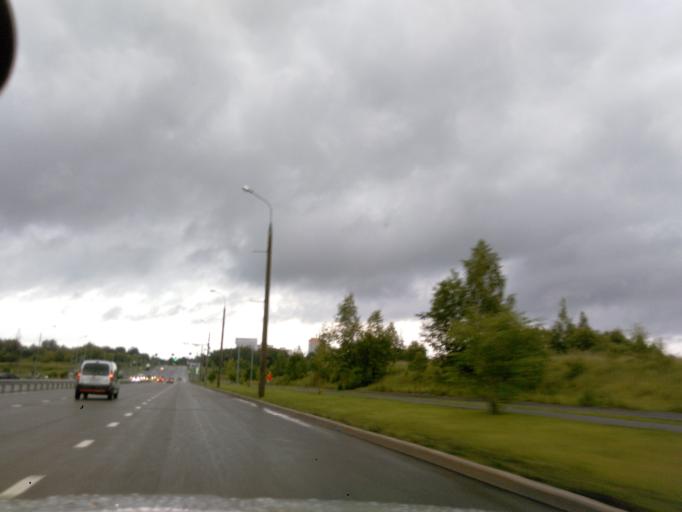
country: RU
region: Moscow
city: Zelenograd
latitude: 55.9700
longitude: 37.1715
